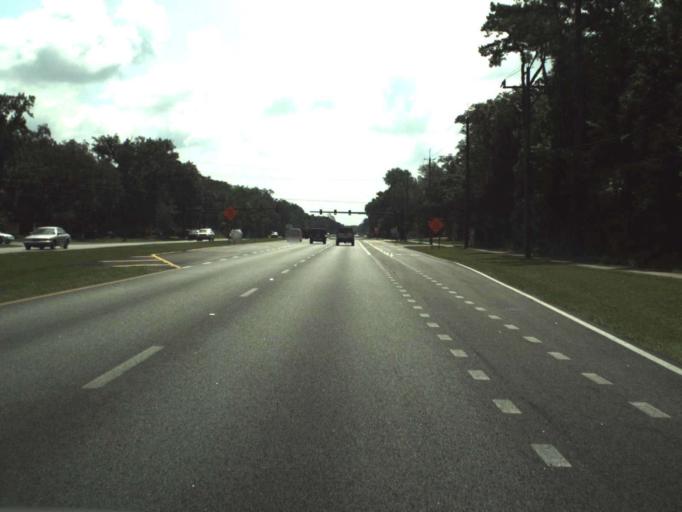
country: US
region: Florida
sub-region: Volusia County
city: Glencoe
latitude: 29.0131
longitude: -80.9664
